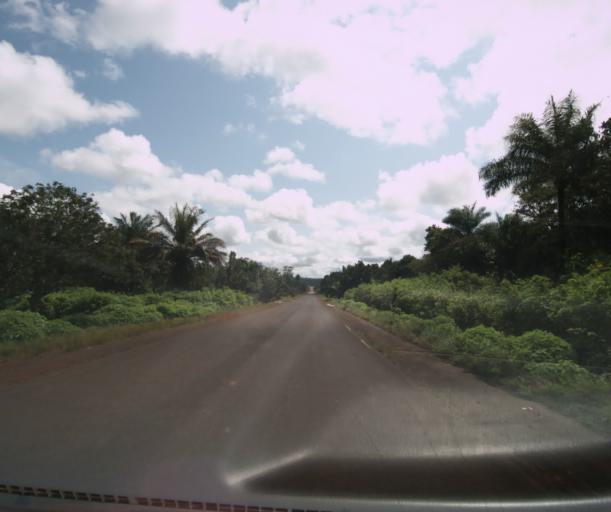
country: CM
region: West
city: Foumban
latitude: 5.6810
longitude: 10.8011
